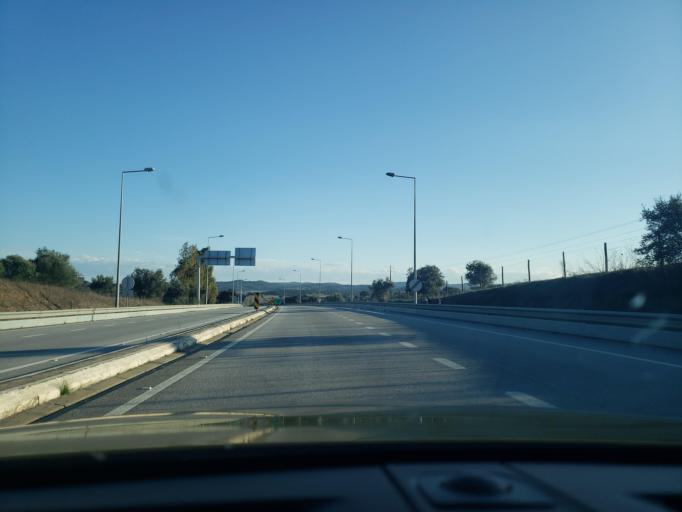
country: PT
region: Evora
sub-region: Portel
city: Portel
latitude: 38.3939
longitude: -7.7178
